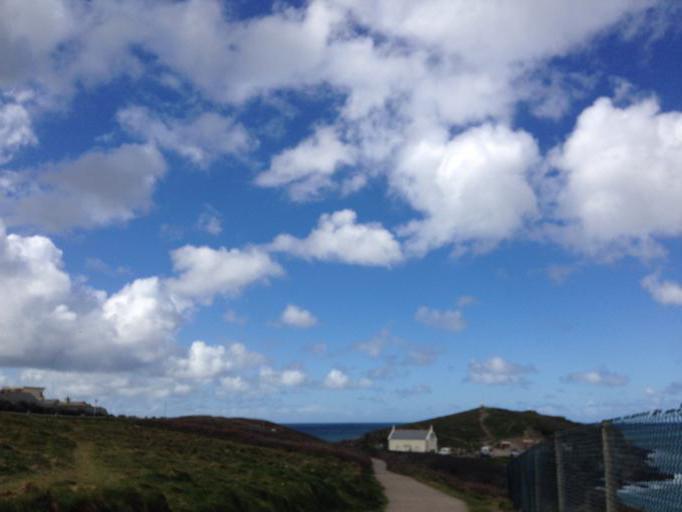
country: GB
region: England
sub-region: Cornwall
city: Newquay
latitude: 50.4214
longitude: -5.0955
